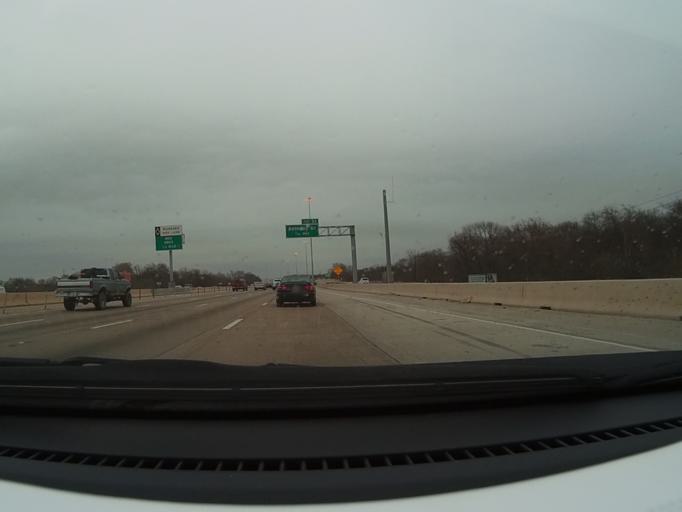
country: US
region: Texas
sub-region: Collin County
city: Allen
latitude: 33.0741
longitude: -96.6866
